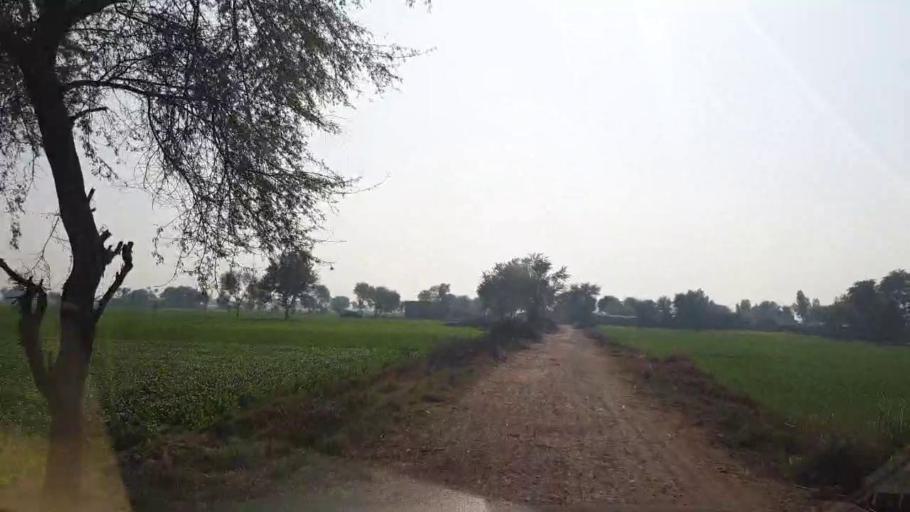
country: PK
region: Sindh
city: Ubauro
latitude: 28.1111
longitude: 69.7938
